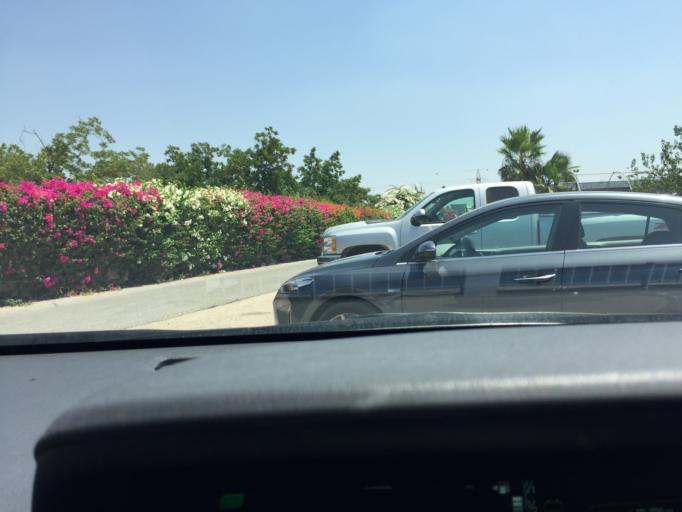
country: IL
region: Central District
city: Yehud
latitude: 32.0433
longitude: 34.9039
